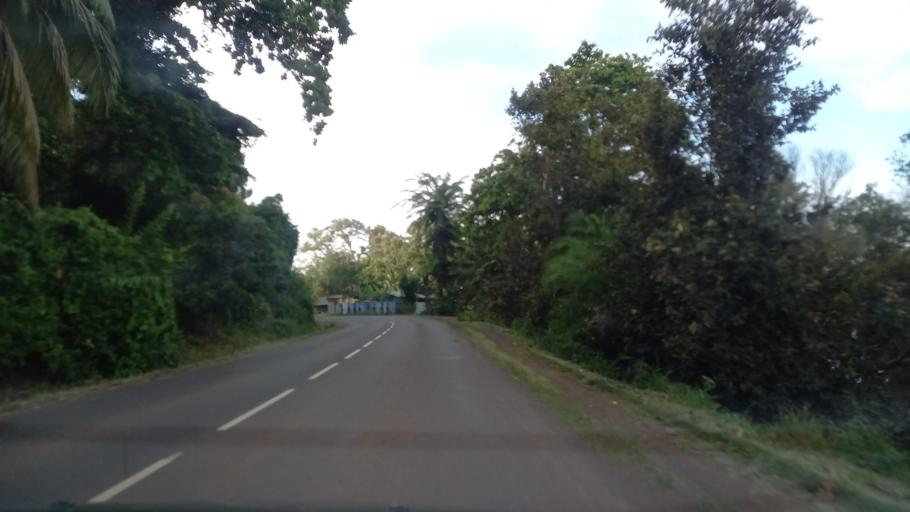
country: YT
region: Bandraboua
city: Bandraboua
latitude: -12.7325
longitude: 45.1373
